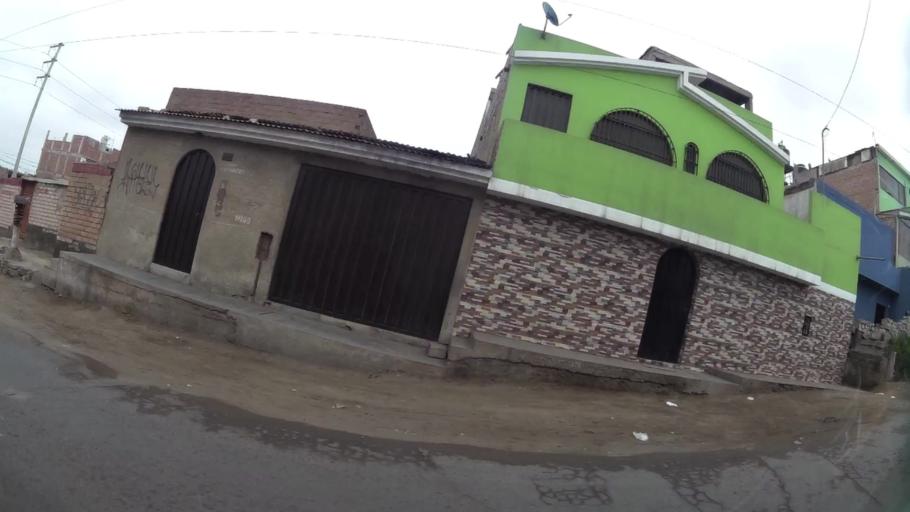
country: PE
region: Lima
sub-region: Lima
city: Surco
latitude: -12.1977
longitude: -76.9860
